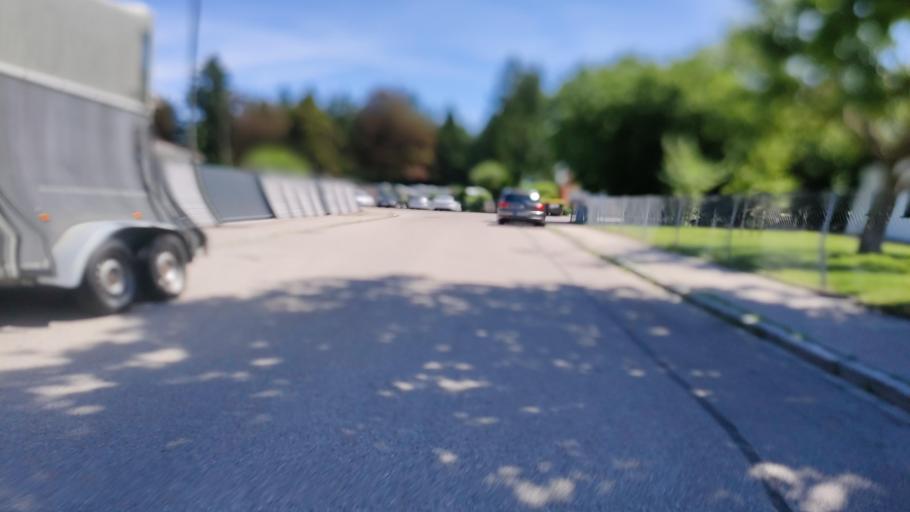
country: DE
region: Bavaria
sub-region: Swabia
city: Bad Worishofen
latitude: 48.0241
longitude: 10.5975
